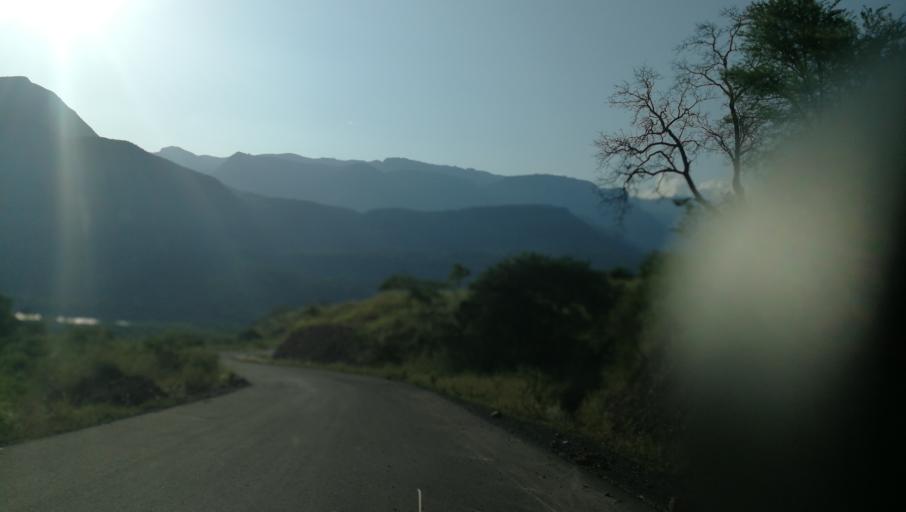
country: ET
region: Southern Nations, Nationalities, and People's Region
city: Areka
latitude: 6.8263
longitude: 37.2978
